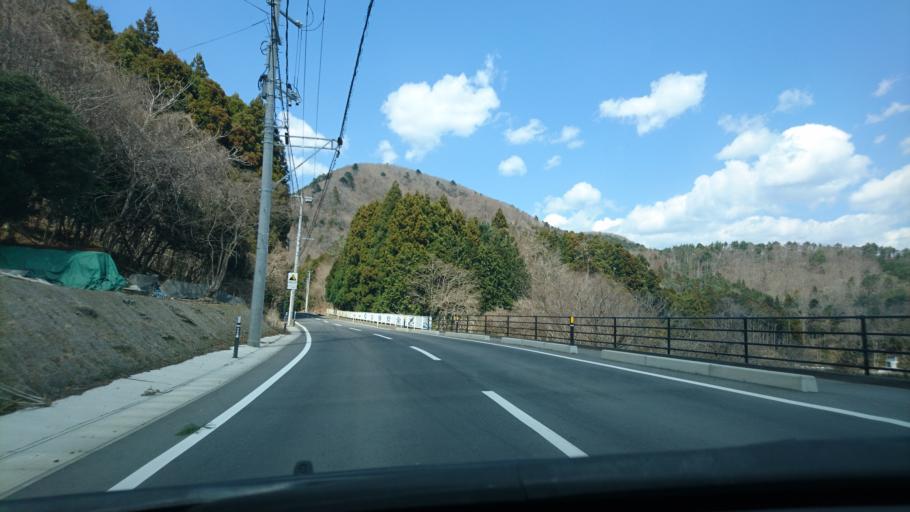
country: JP
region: Miyagi
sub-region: Oshika Gun
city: Onagawa Cho
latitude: 38.4663
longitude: 141.4737
